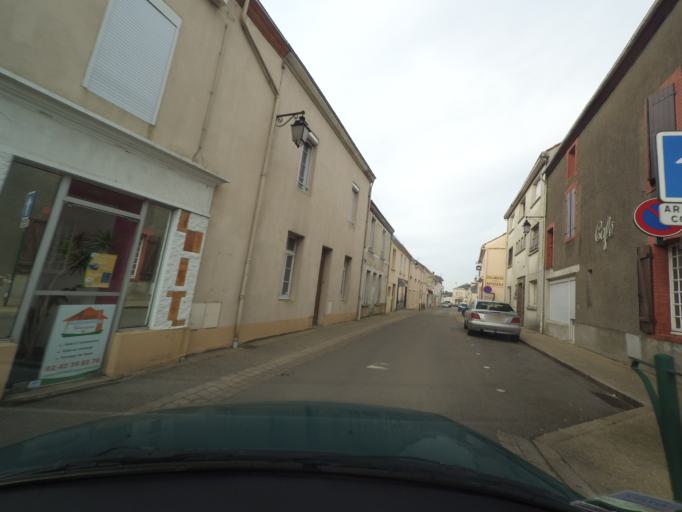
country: FR
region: Pays de la Loire
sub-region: Departement de la Loire-Atlantique
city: Saint-Pere-en-Retz
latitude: 47.2061
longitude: -2.0442
